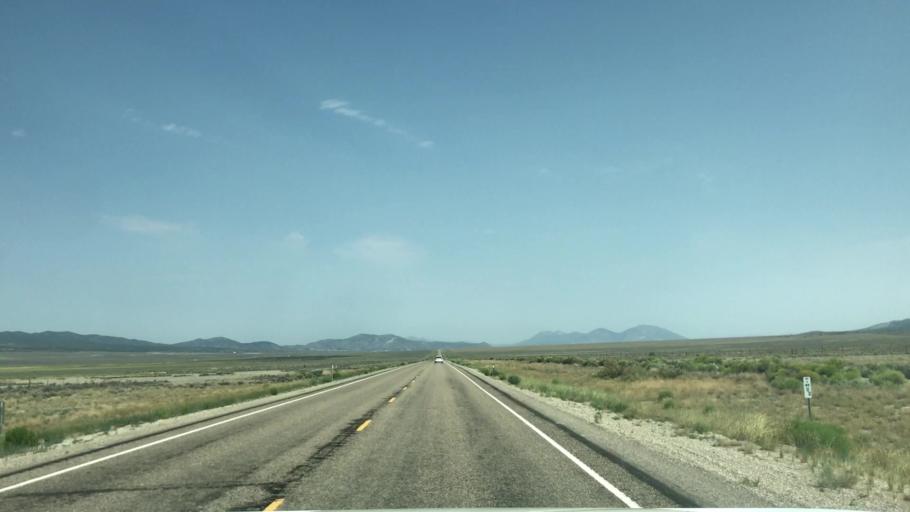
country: US
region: Nevada
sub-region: White Pine County
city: Ely
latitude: 39.1097
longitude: -114.7669
